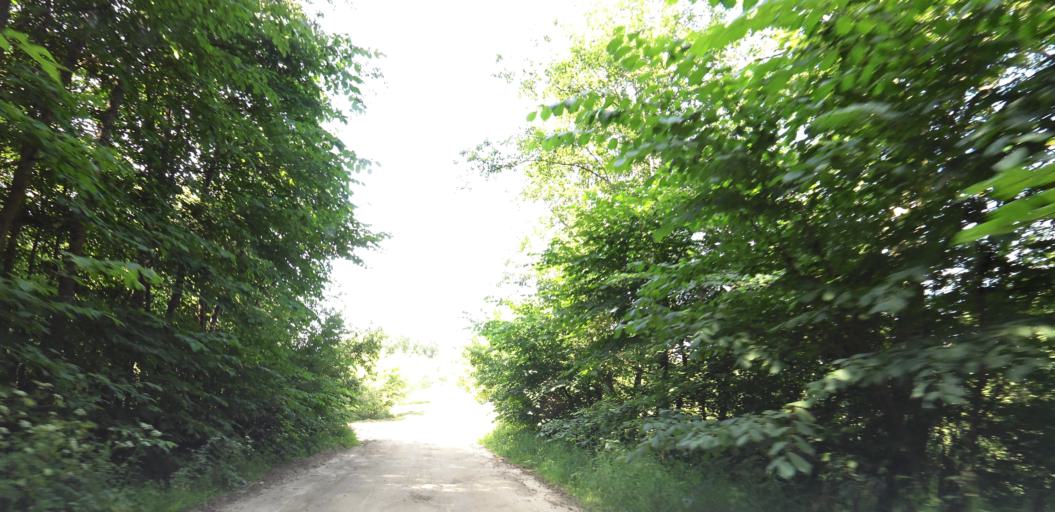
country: LT
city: Grigiskes
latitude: 54.7742
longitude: 25.0622
